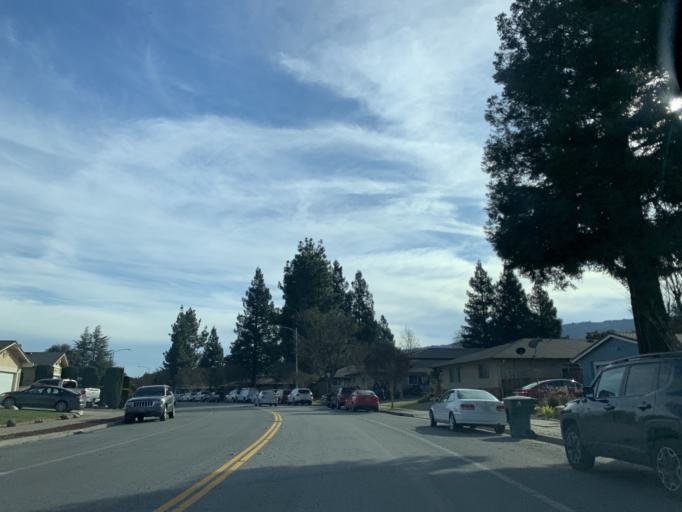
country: US
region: California
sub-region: Santa Clara County
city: Gilroy
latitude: 37.0163
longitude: -121.5948
